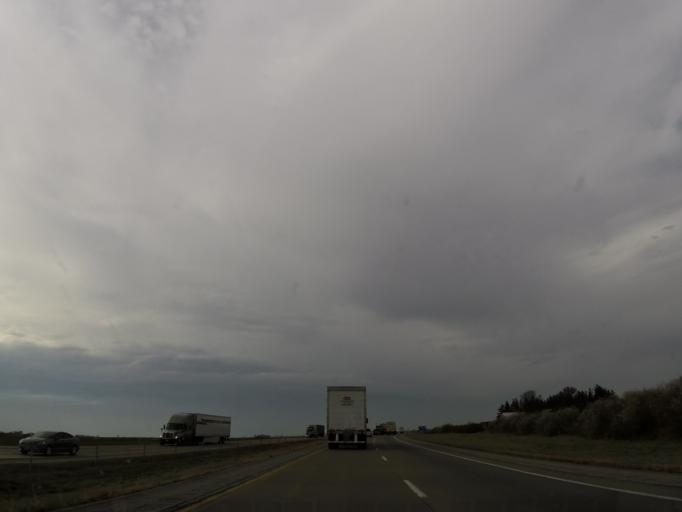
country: US
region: Iowa
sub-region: Scott County
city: Walcott
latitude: 41.6040
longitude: -90.7221
